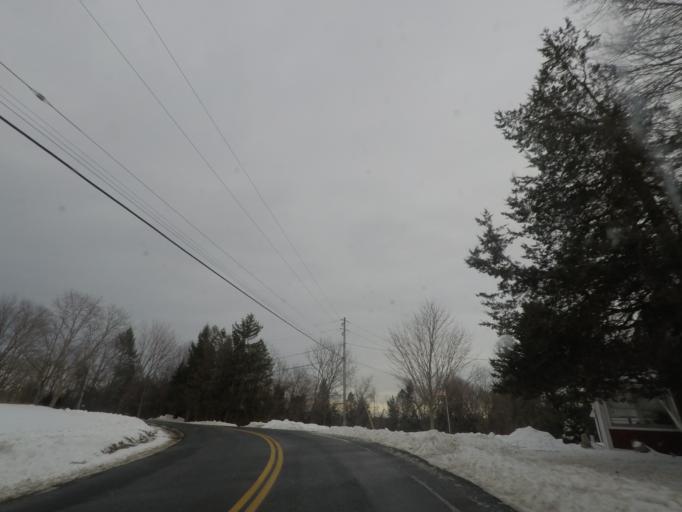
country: US
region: New York
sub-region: Rensselaer County
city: Castleton-on-Hudson
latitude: 42.5125
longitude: -73.7157
